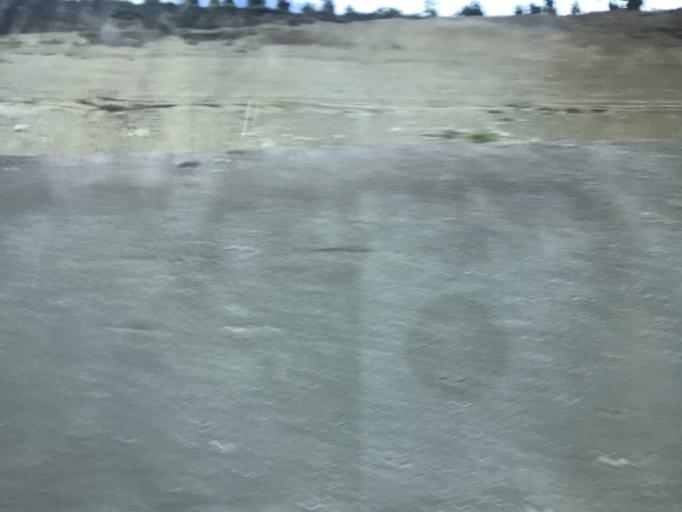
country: GT
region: Chimaltenango
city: Parramos
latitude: 14.6258
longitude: -90.7987
